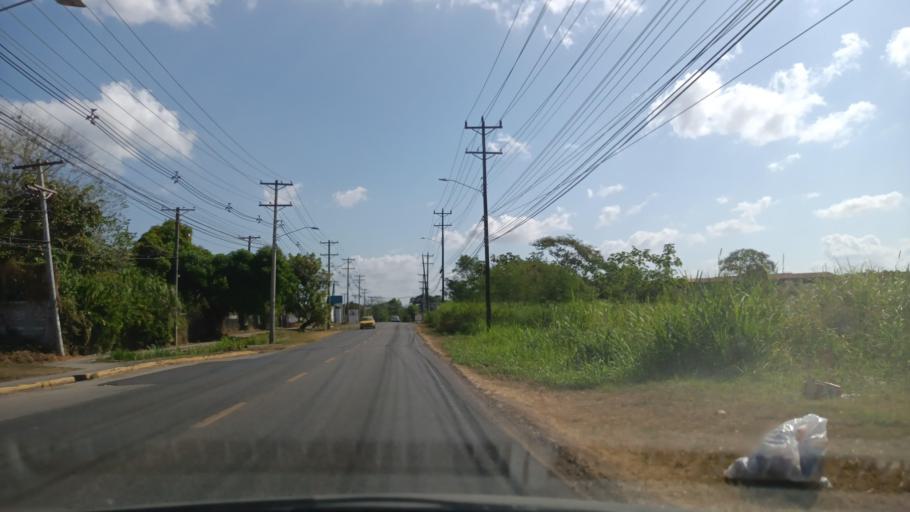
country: PA
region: Panama
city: Tocumen
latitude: 9.0791
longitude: -79.4085
